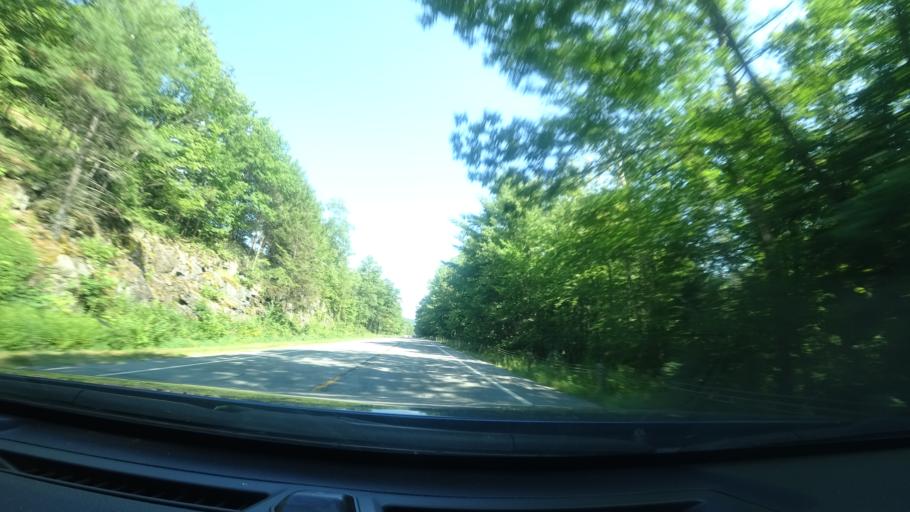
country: US
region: New York
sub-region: Warren County
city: Warrensburg
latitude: 43.5970
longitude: -73.8011
